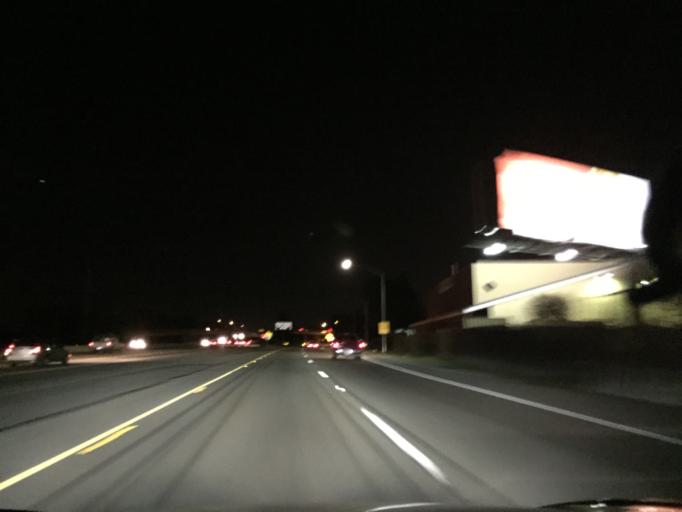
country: US
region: California
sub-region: Alameda County
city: San Lorenzo
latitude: 37.6928
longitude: -122.1415
